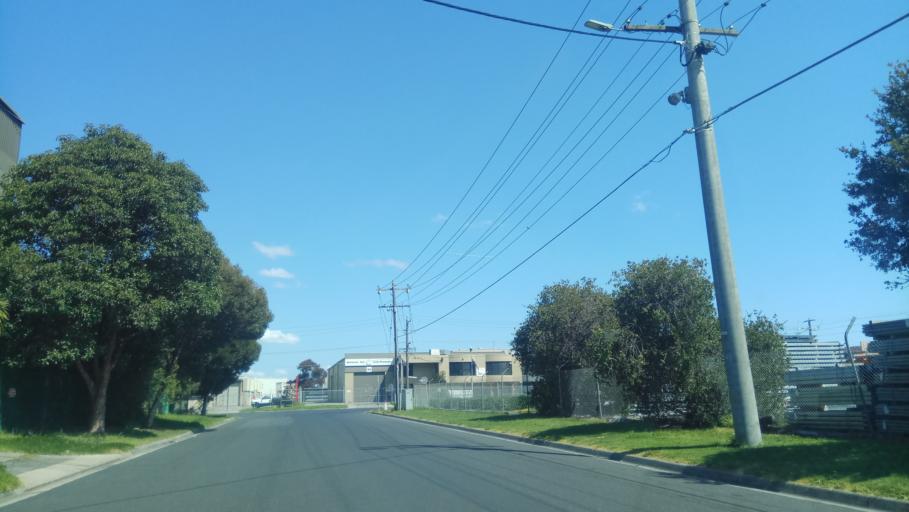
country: AU
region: Victoria
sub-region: Kingston
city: Dingley Village
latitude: -37.9889
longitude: 145.1155
